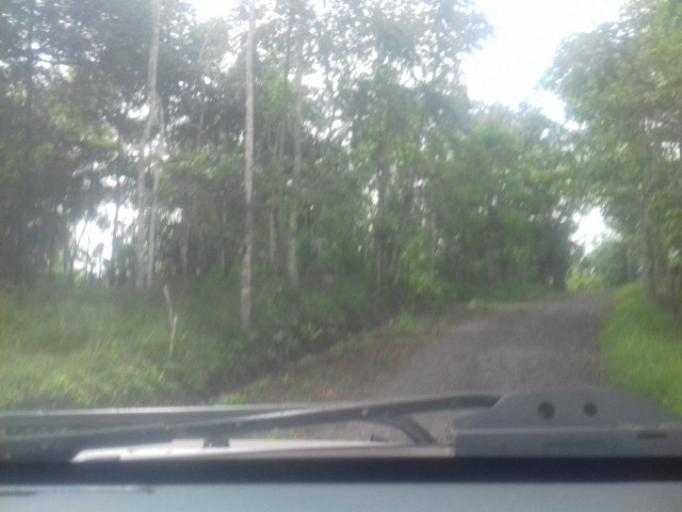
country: NI
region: Atlantico Norte (RAAN)
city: Waslala
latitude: 13.5016
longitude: -85.2325
